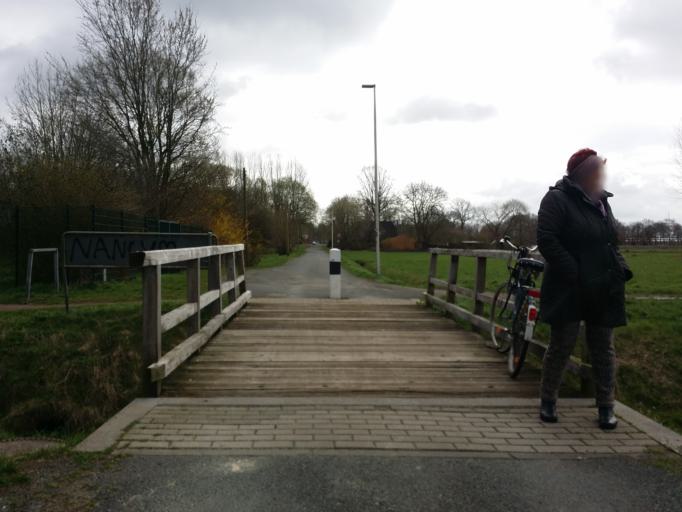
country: DE
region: Lower Saxony
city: Delmenhorst
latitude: 53.0207
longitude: 8.6321
